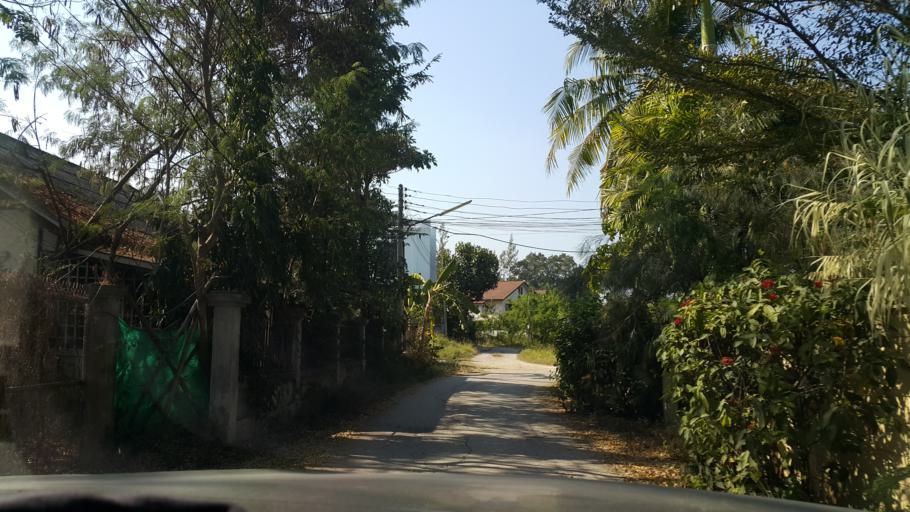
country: TH
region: Chiang Mai
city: Chiang Mai
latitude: 18.7672
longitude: 99.0249
